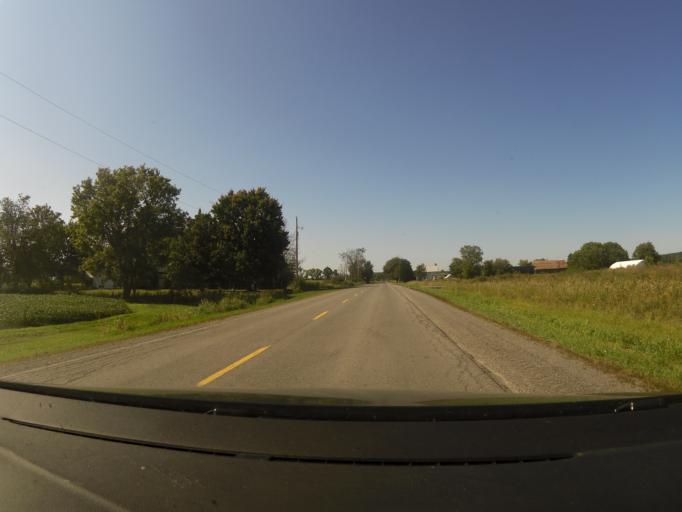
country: CA
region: Ontario
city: Carleton Place
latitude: 45.3575
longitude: -76.0965
